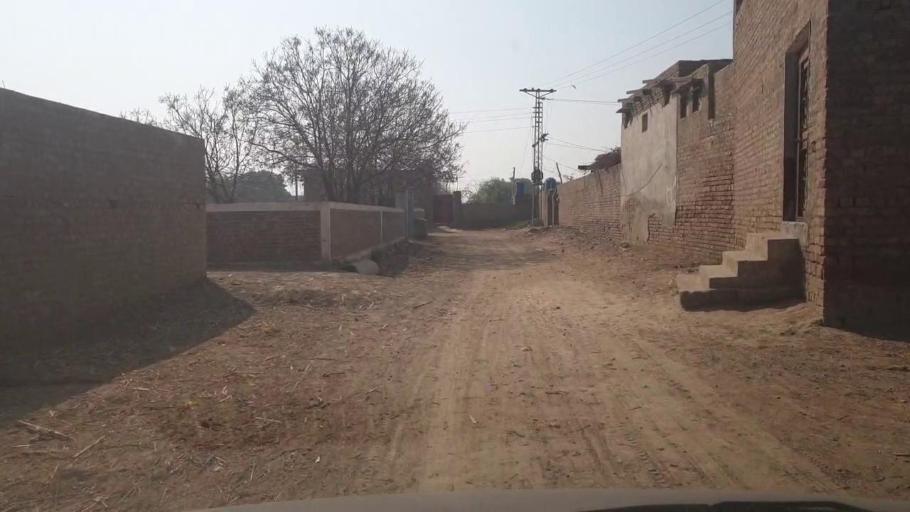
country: PK
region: Sindh
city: Tando Allahyar
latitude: 25.4591
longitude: 68.7822
